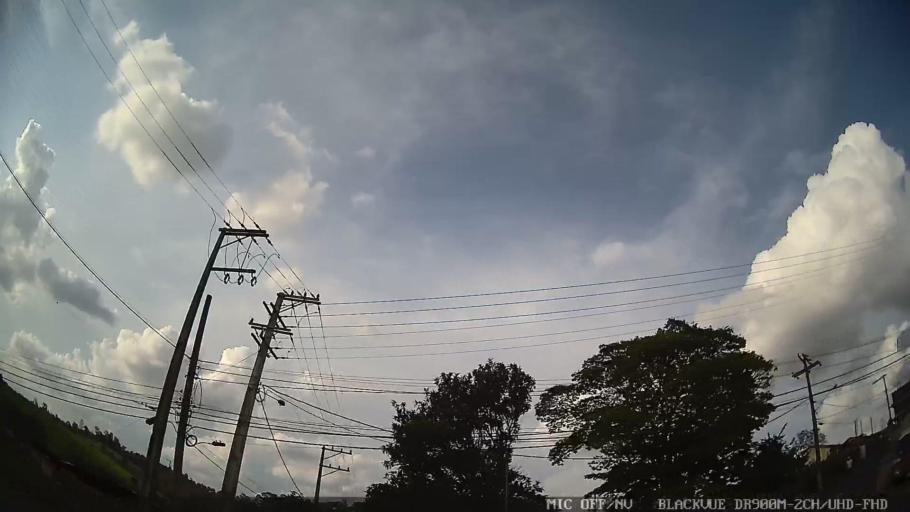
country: BR
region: Sao Paulo
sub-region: Braganca Paulista
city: Braganca Paulista
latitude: -22.9340
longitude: -46.5111
